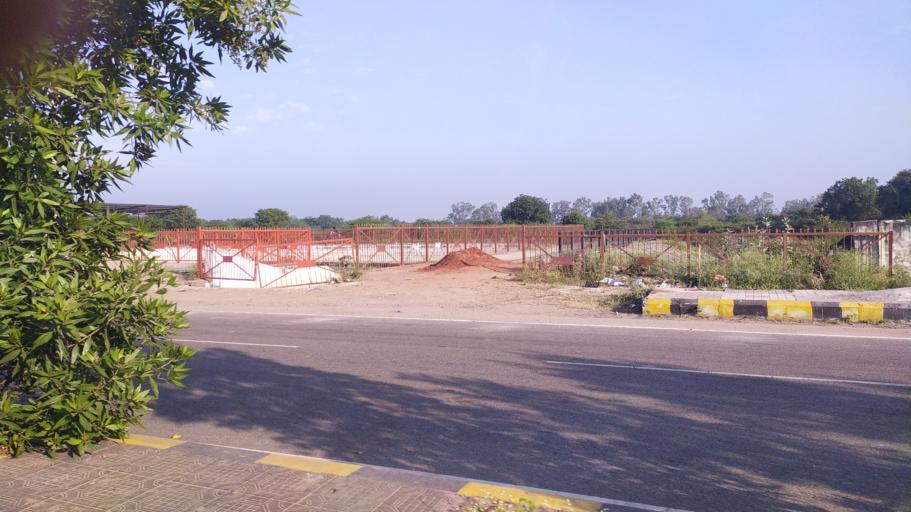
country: IN
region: Telangana
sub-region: Hyderabad
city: Hyderabad
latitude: 17.3197
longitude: 78.3910
